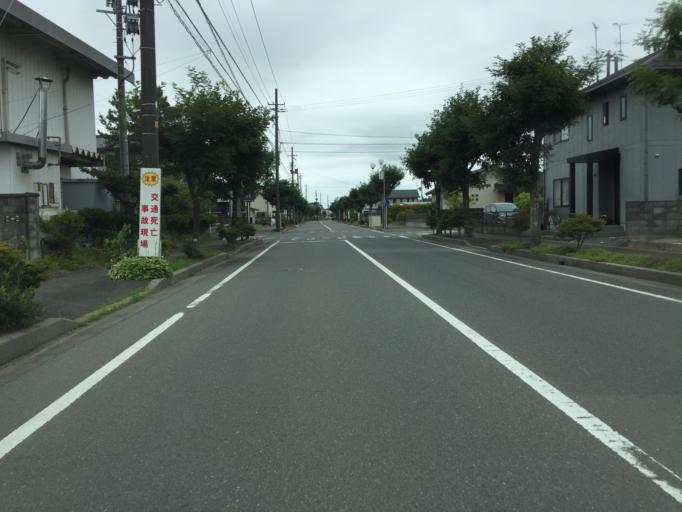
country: JP
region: Fukushima
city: Namie
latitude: 37.7078
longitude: 140.9610
